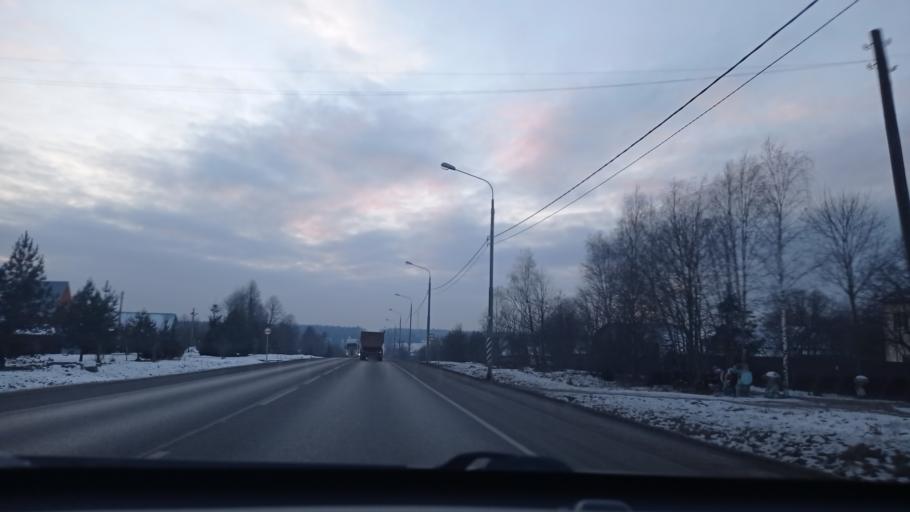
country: RU
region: Kaluga
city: Zhukovo
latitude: 55.1482
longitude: 36.8083
